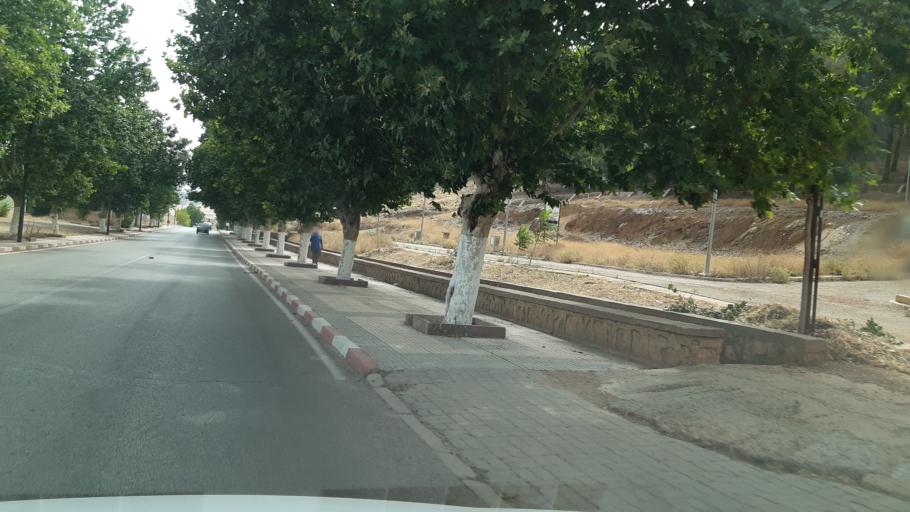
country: MA
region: Meknes-Tafilalet
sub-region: Ifrane
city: Azrou
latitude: 33.4382
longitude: -5.2163
